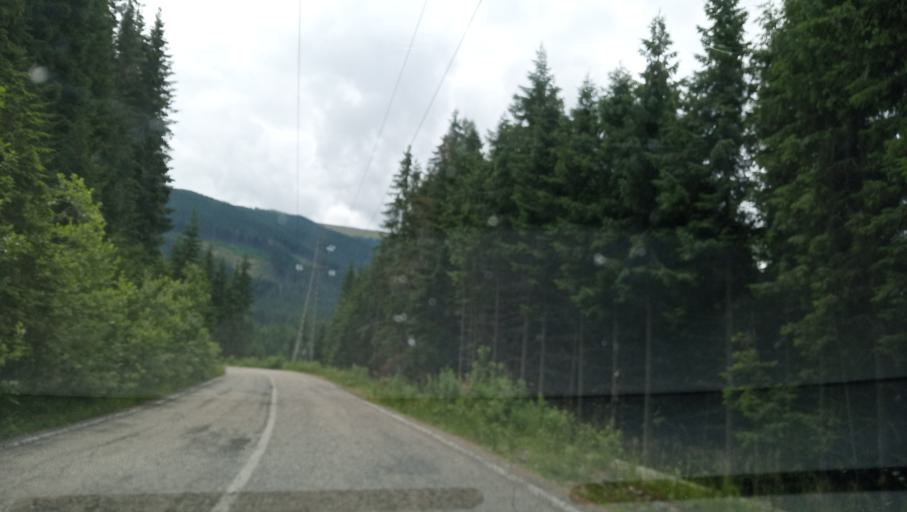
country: RO
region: Valcea
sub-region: Comuna Voineasa
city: Voineasa
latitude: 45.4250
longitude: 23.7383
